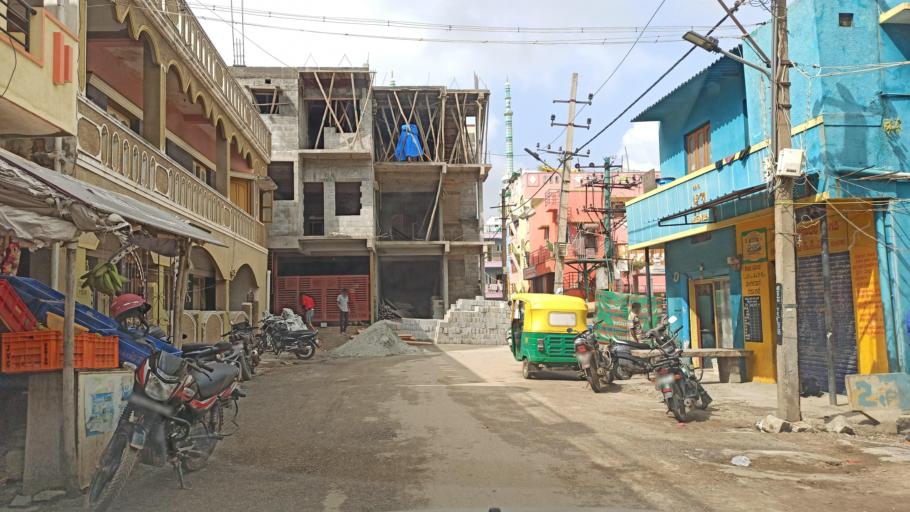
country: IN
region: Karnataka
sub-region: Bangalore Urban
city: Bangalore
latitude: 13.0026
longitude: 77.6718
